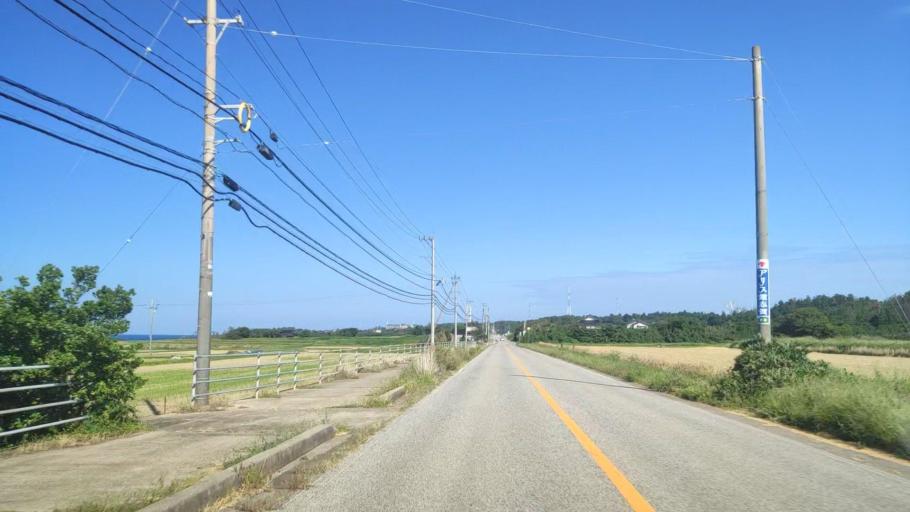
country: JP
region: Ishikawa
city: Hakui
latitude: 37.0414
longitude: 136.7410
